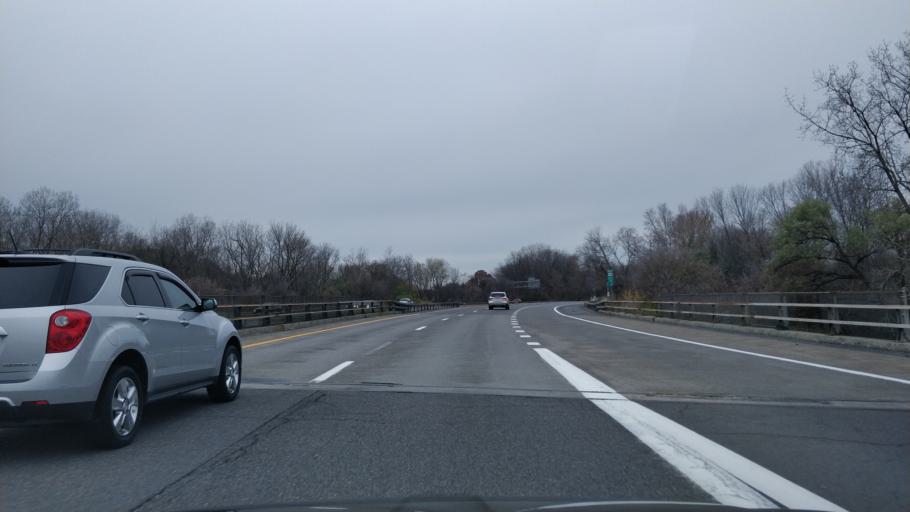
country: US
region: New York
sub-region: Onondaga County
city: North Syracuse
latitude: 43.1423
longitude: -76.1174
